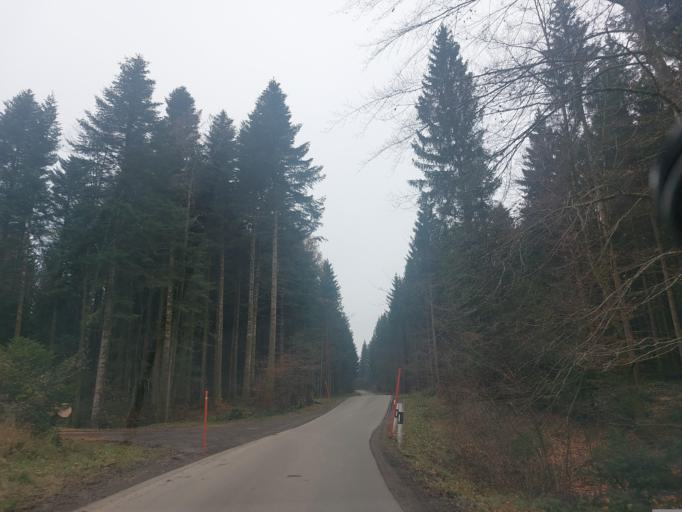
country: CH
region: Vaud
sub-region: Lavaux-Oron District
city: Palezieux
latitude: 46.5644
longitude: 6.8619
